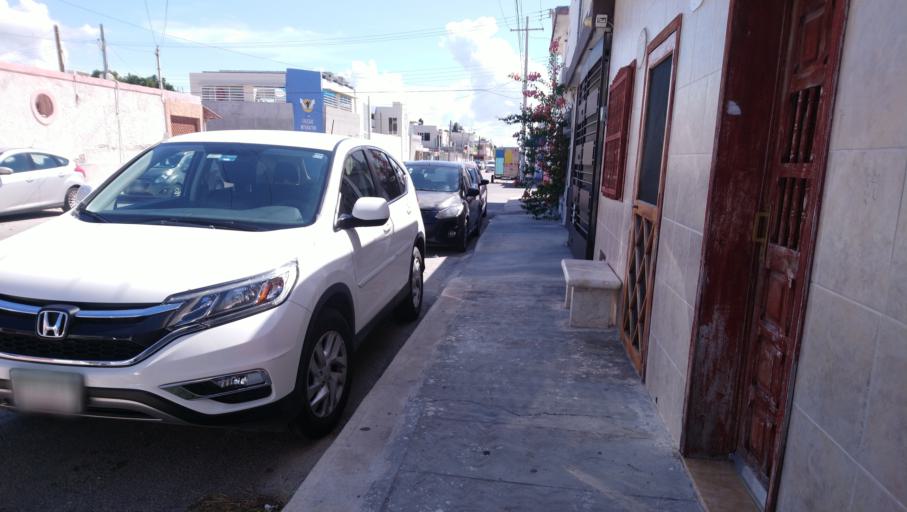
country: MX
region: Yucatan
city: Progreso de Castro
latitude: 21.2837
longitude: -89.6710
